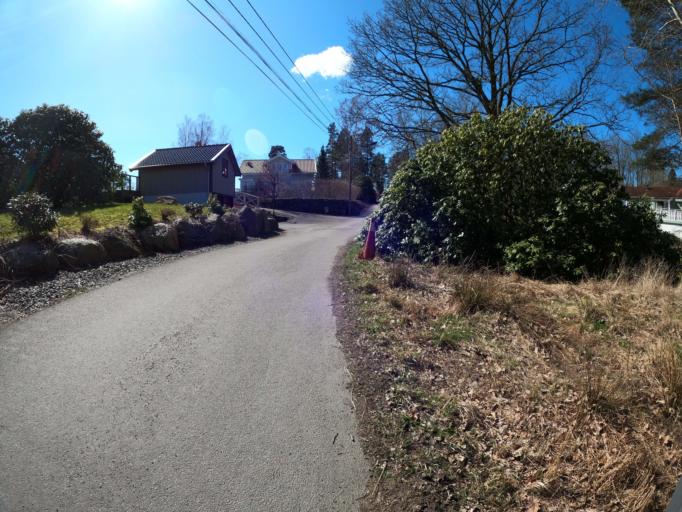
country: SE
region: Vaestra Goetaland
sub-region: Harryda Kommun
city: Molnlycke
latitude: 57.6346
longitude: 12.1251
